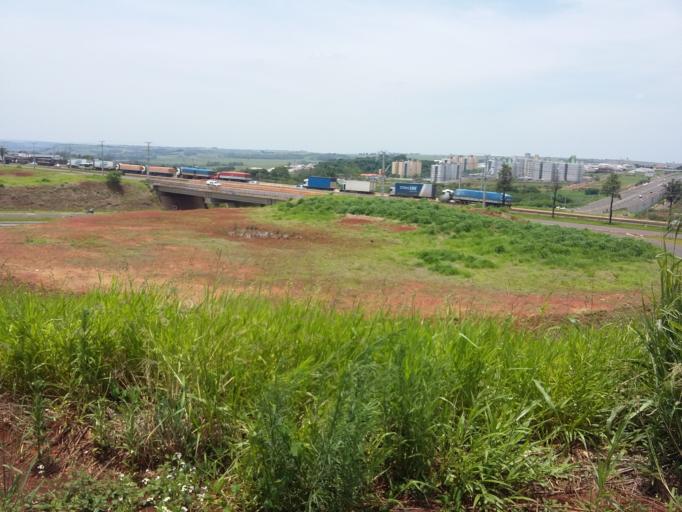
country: BR
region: Parana
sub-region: Maringa
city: Maringa
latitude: -23.3806
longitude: -51.9147
